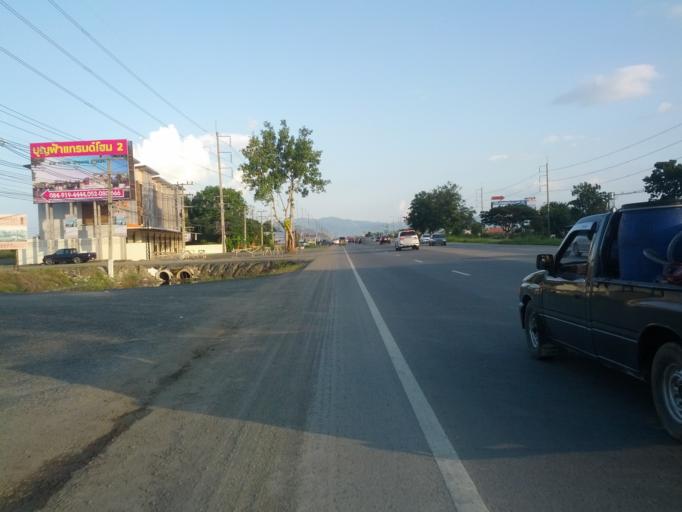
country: TH
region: Chiang Mai
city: San Kamphaeng
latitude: 18.7437
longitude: 99.0762
